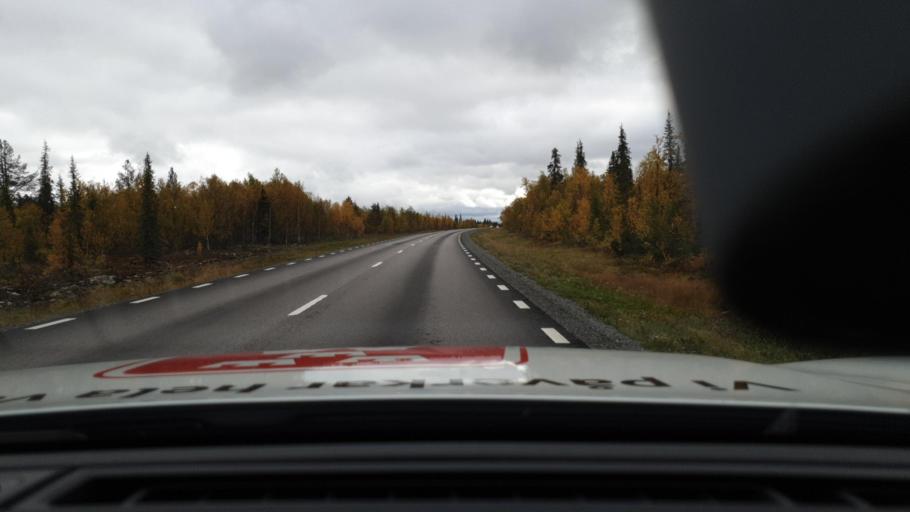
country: SE
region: Norrbotten
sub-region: Gallivare Kommun
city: Malmberget
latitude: 67.5768
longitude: 21.1383
